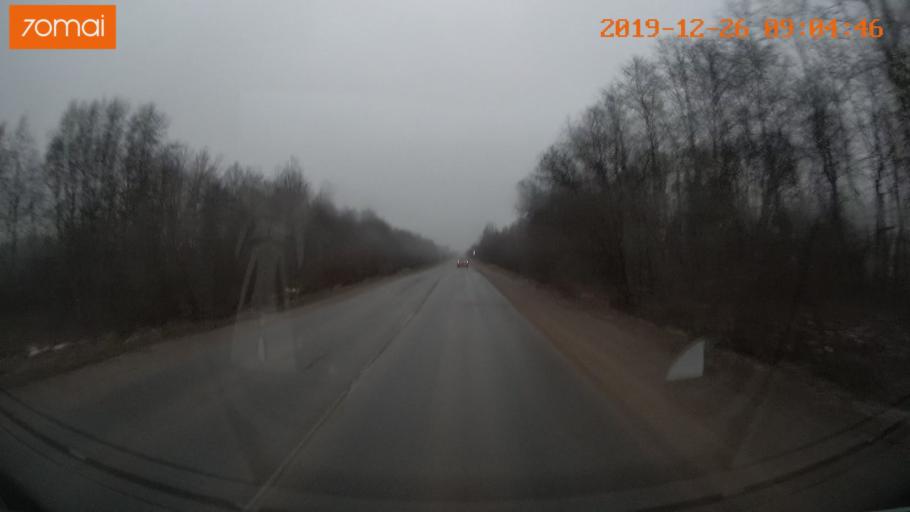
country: RU
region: Vologda
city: Gryazovets
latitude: 58.8181
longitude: 40.2614
